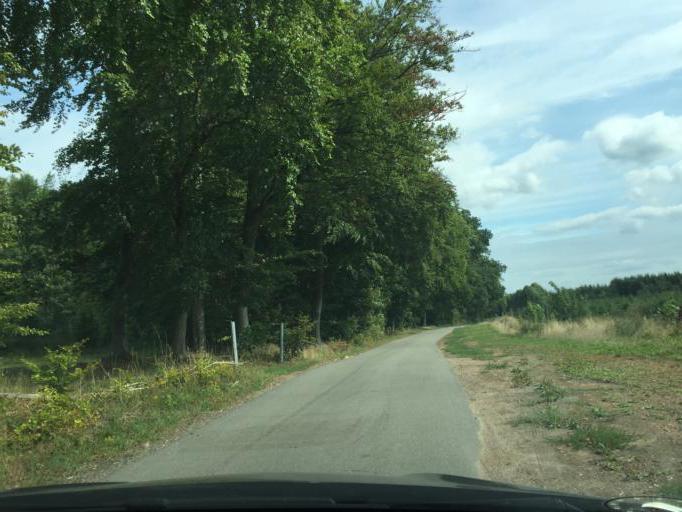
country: DK
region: South Denmark
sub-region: Assens Kommune
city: Tommerup Stationsby
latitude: 55.4150
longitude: 10.2116
